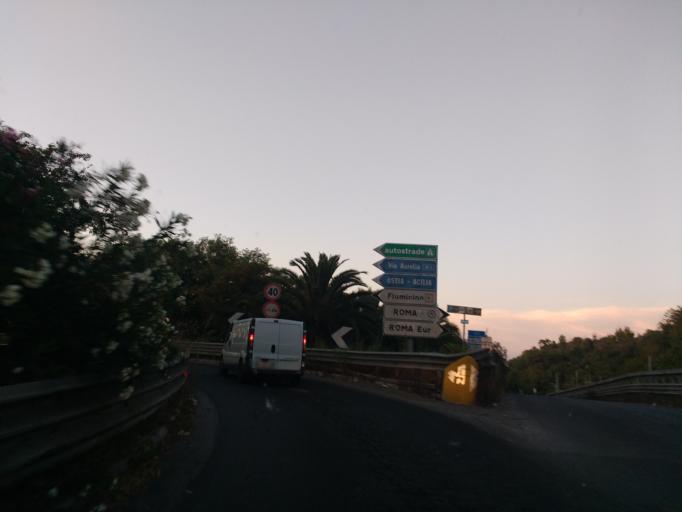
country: IT
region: Latium
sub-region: Citta metropolitana di Roma Capitale
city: Vitinia
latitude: 41.8105
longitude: 12.4238
